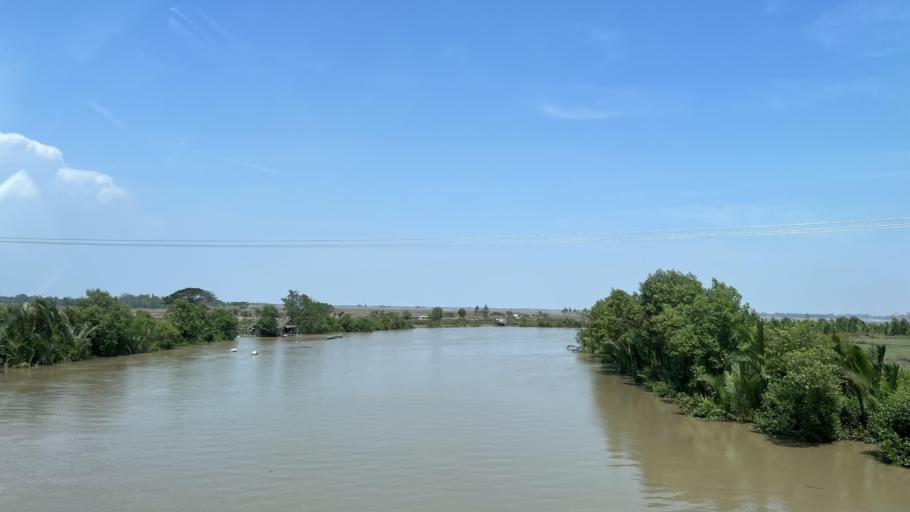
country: MM
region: Ayeyarwady
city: Pyapon
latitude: 16.0152
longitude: 95.6039
